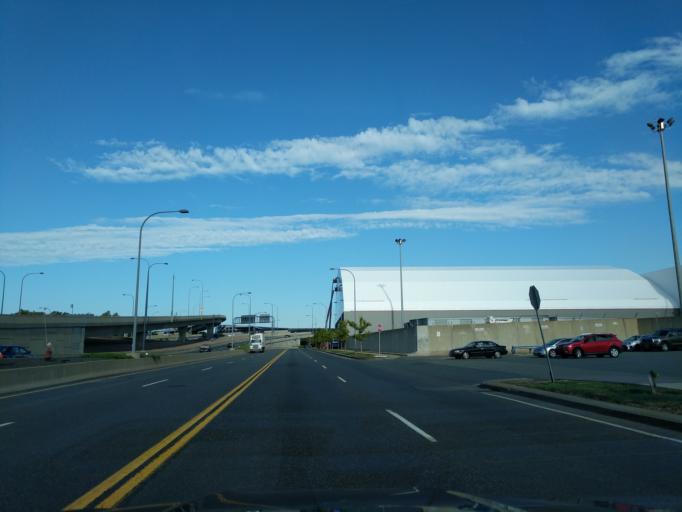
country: US
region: Massachusetts
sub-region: Suffolk County
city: Chelsea
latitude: 42.3721
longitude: -71.0275
